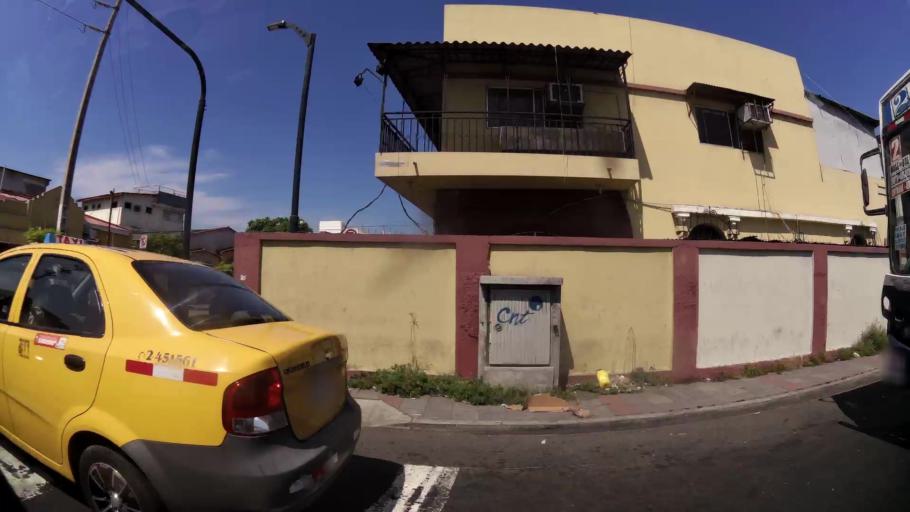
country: EC
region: Guayas
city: Guayaquil
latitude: -2.1844
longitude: -79.8931
